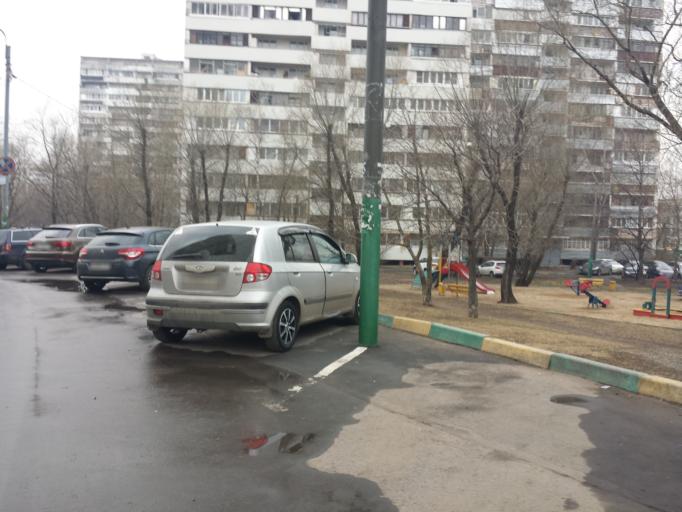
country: RU
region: Moskovskaya
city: Novogireyevo
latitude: 55.7531
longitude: 37.8215
